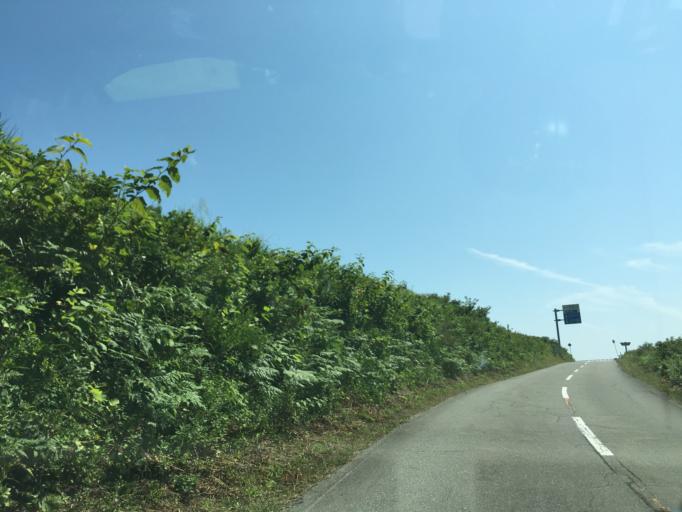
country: JP
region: Akita
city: Tenno
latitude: 39.9319
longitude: 139.8729
